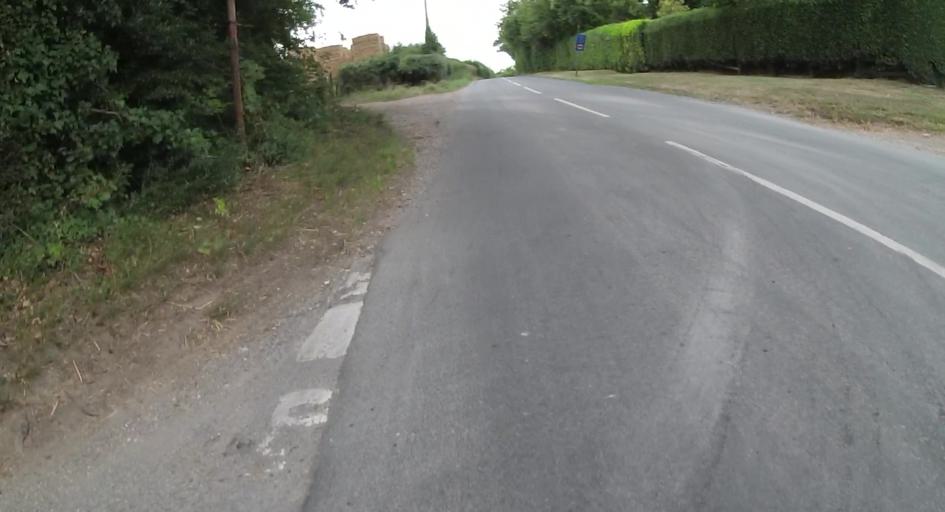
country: GB
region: England
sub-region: Hampshire
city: Kings Worthy
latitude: 51.1241
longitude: -1.3103
